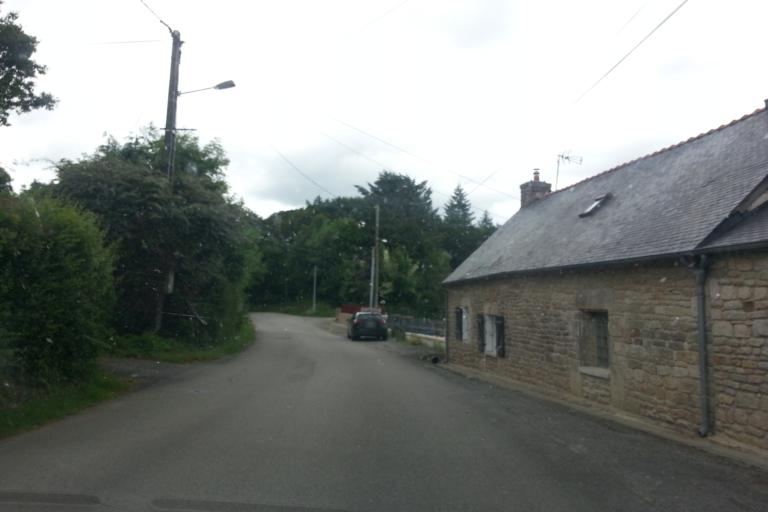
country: FR
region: Brittany
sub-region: Departement du Morbihan
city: Le Faouet
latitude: 48.0437
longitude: -3.4949
